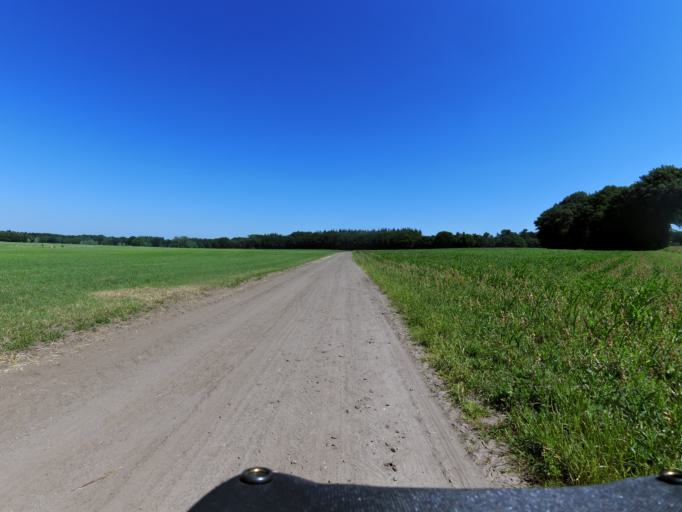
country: NL
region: Overijssel
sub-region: Gemeente Twenterand
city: Den Ham
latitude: 52.5030
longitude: 6.4326
